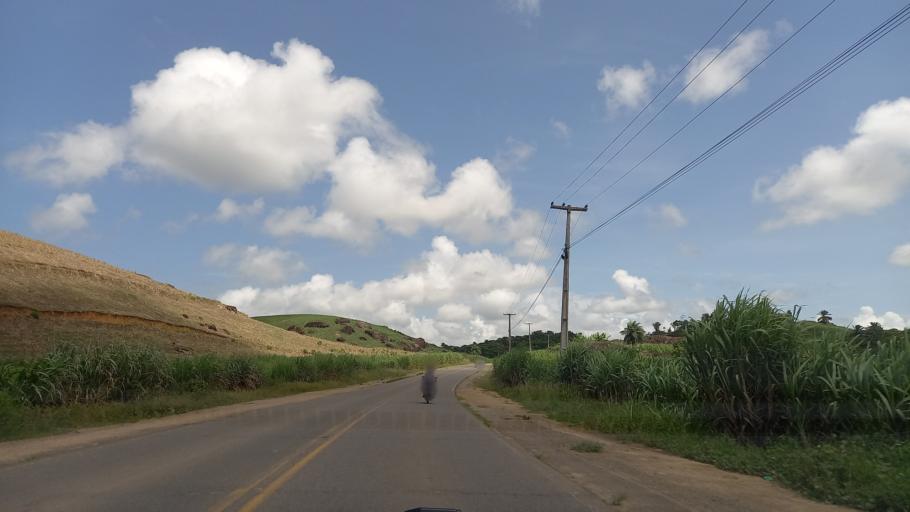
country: BR
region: Pernambuco
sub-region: Sirinhaem
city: Sirinhaem
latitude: -8.6083
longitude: -35.1176
